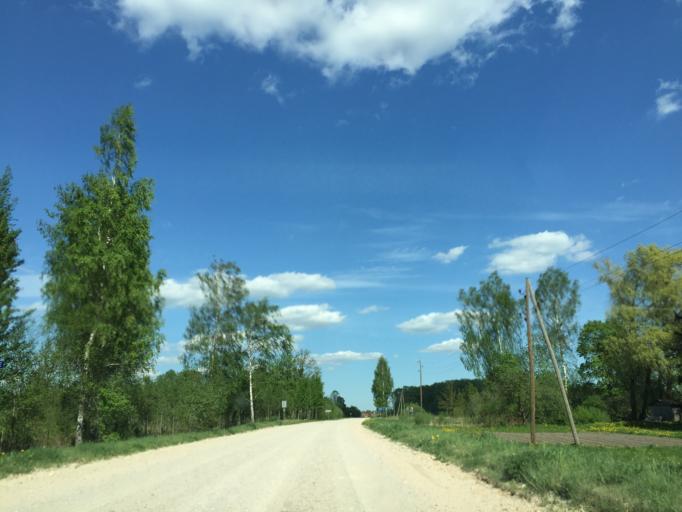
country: LV
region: Bauskas Rajons
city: Bauska
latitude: 56.3912
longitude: 24.0979
